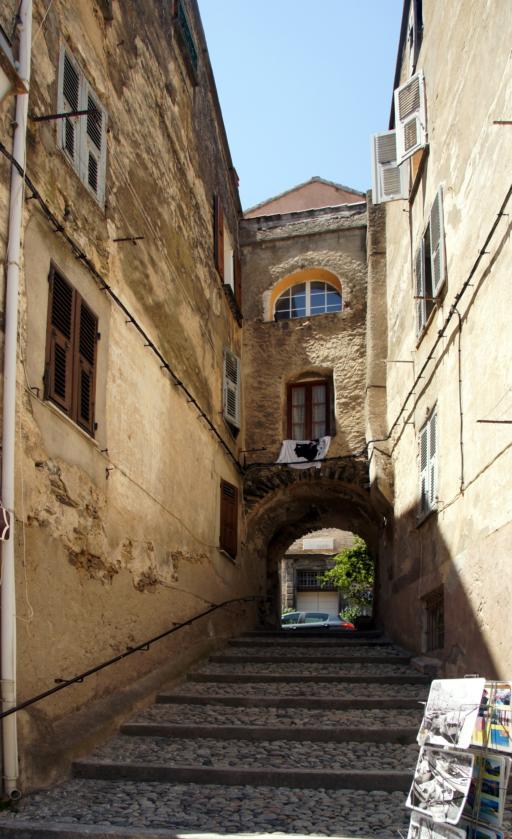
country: FR
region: Corsica
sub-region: Departement de la Haute-Corse
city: Corte
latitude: 42.3050
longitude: 9.1497
